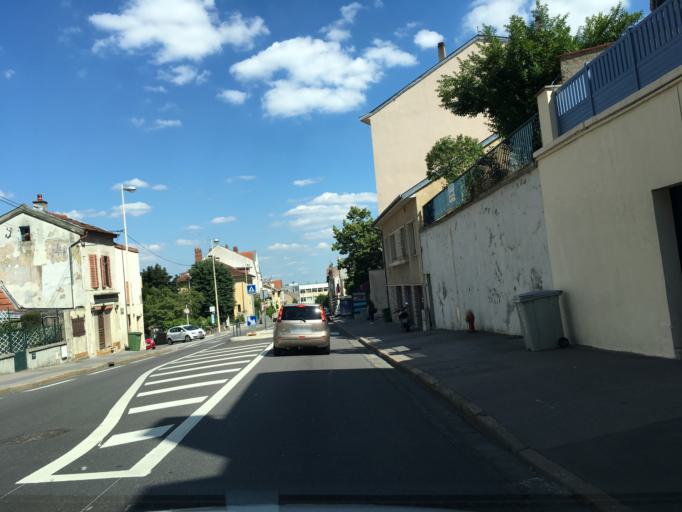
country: FR
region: Lorraine
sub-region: Departement de Meurthe-et-Moselle
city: Maxeville
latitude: 48.6964
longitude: 6.1617
